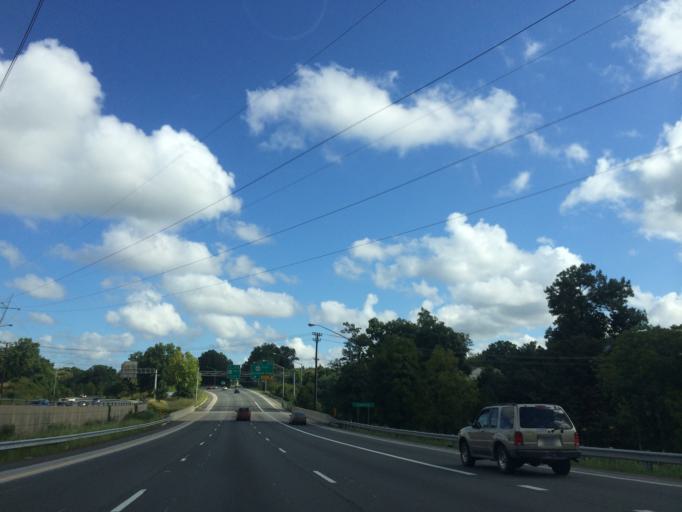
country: US
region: Maryland
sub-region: Howard County
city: Ellicott City
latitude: 39.2693
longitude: -76.8182
